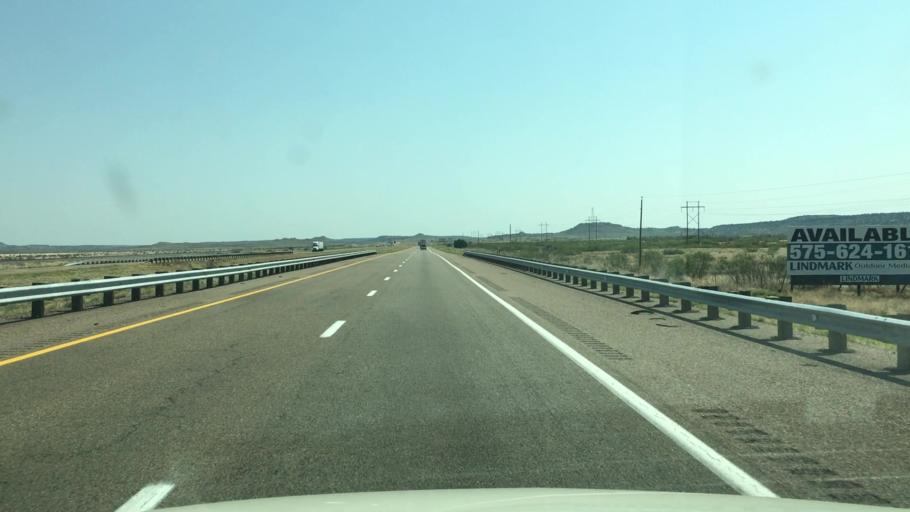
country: US
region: New Mexico
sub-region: Quay County
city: Tucumcari
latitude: 35.1170
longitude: -103.9845
